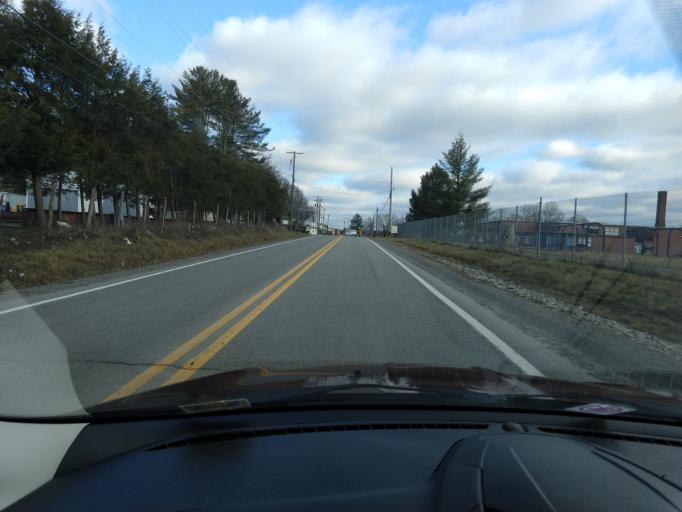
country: US
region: West Virginia
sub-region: Randolph County
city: Elkins
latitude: 38.7879
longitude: -79.9057
